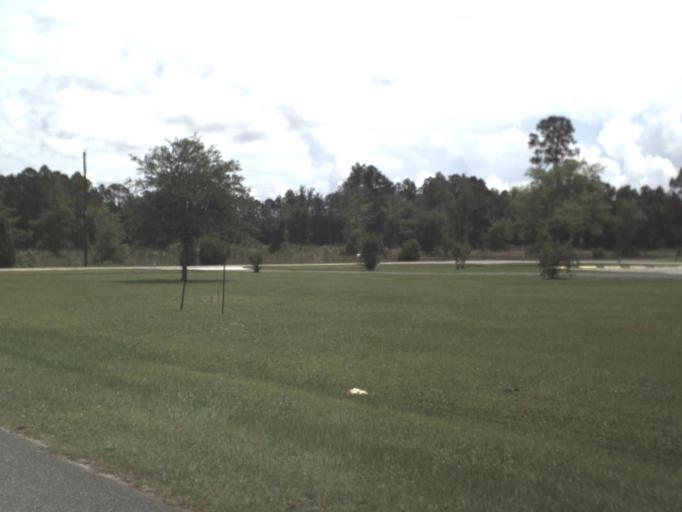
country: US
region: Florida
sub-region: Nassau County
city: Yulee
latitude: 30.6413
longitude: -81.6122
